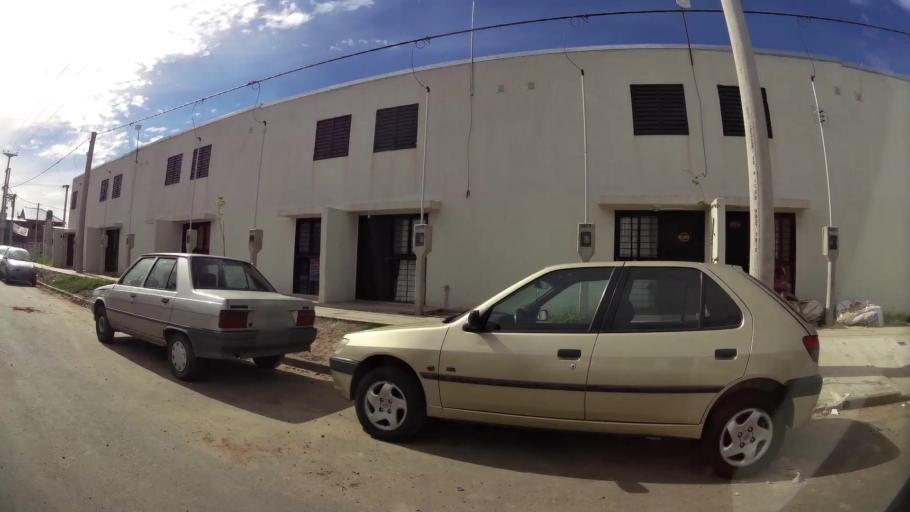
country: AR
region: Santa Fe
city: Granadero Baigorria
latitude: -32.9114
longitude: -60.7171
